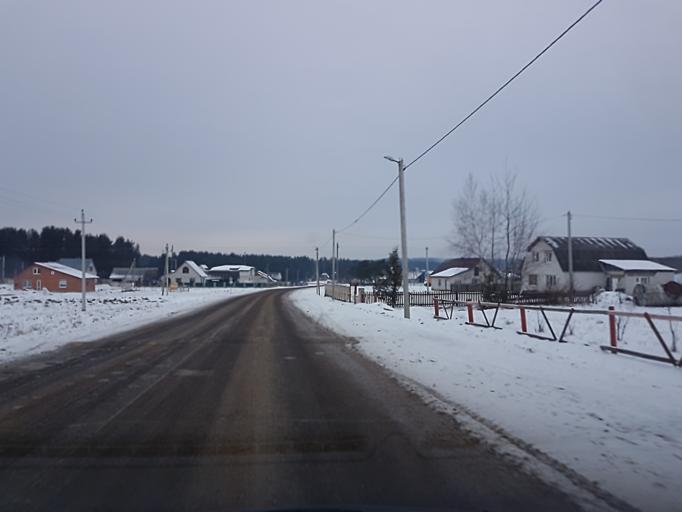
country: BY
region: Minsk
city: Rakaw
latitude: 53.9636
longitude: 27.0403
